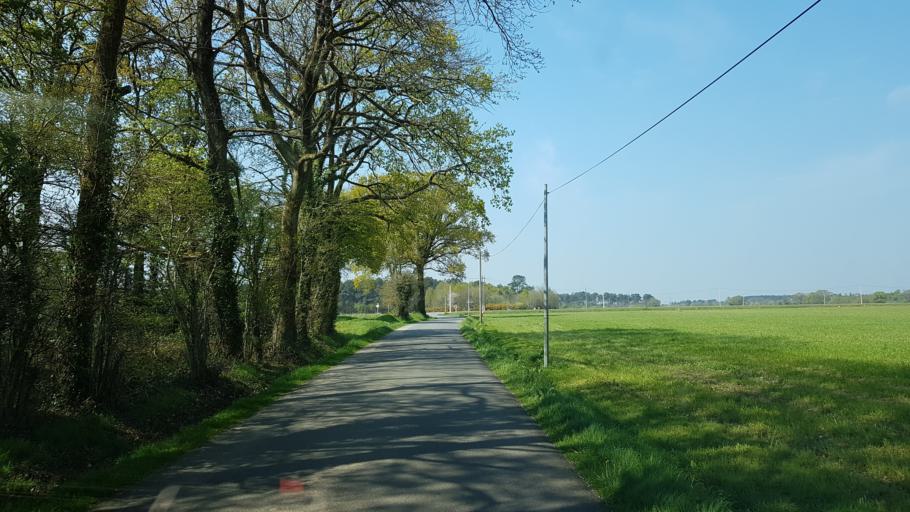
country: FR
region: Brittany
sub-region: Departement du Morbihan
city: Peaule
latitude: 47.5858
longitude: -2.3742
